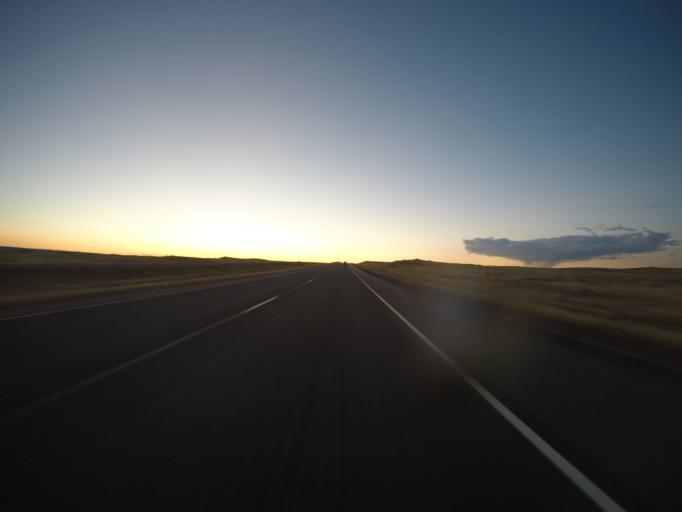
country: US
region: Wyoming
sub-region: Albany County
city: Laramie
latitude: 41.0212
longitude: -105.4225
